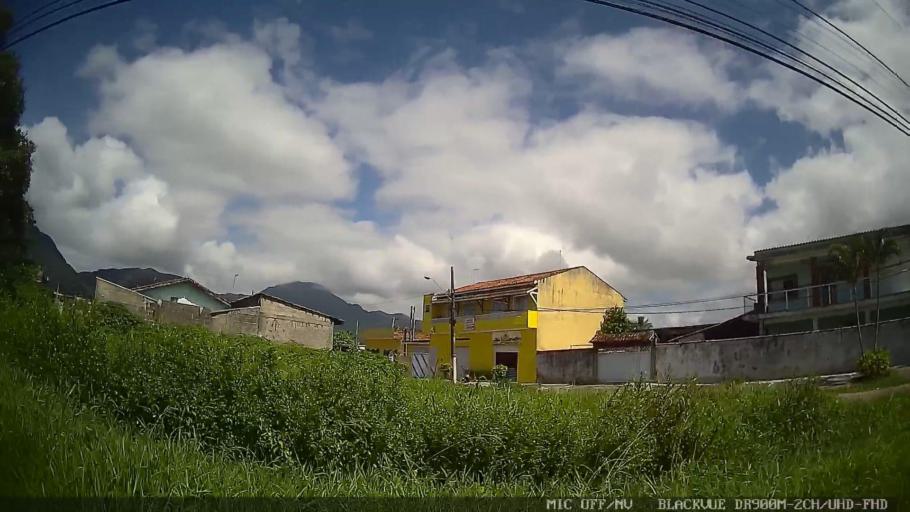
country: BR
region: Sao Paulo
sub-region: Peruibe
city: Peruibe
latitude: -24.3139
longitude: -47.0099
